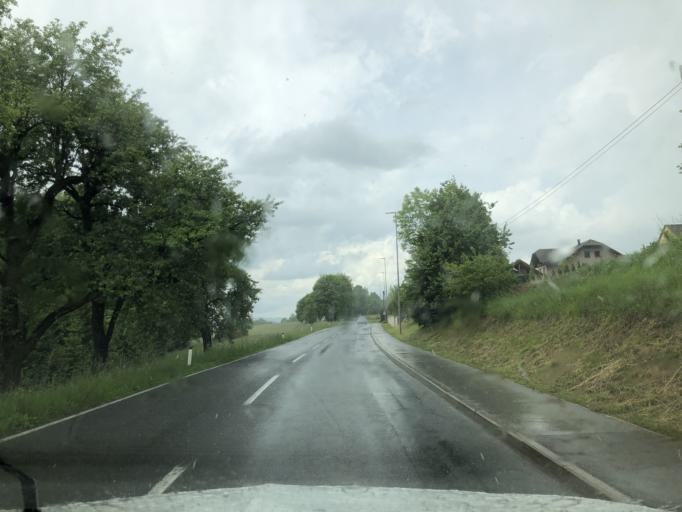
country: SI
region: Cerknica
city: Cerknica
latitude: 45.7781
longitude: 14.3982
